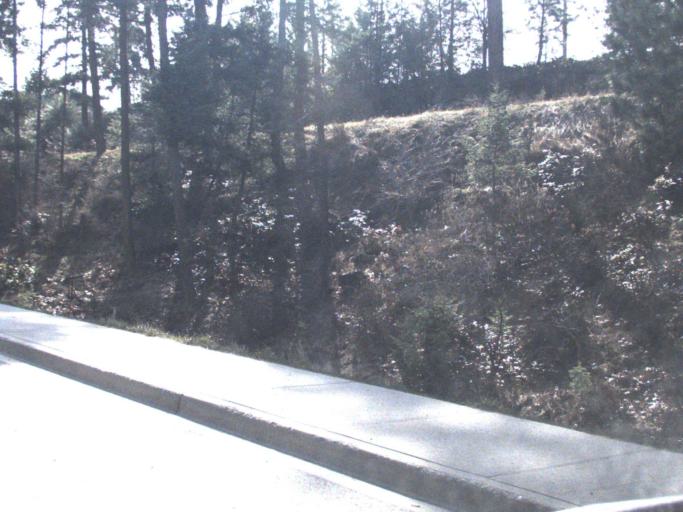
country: US
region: Washington
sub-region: Stevens County
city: Colville
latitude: 48.5469
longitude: -117.8868
